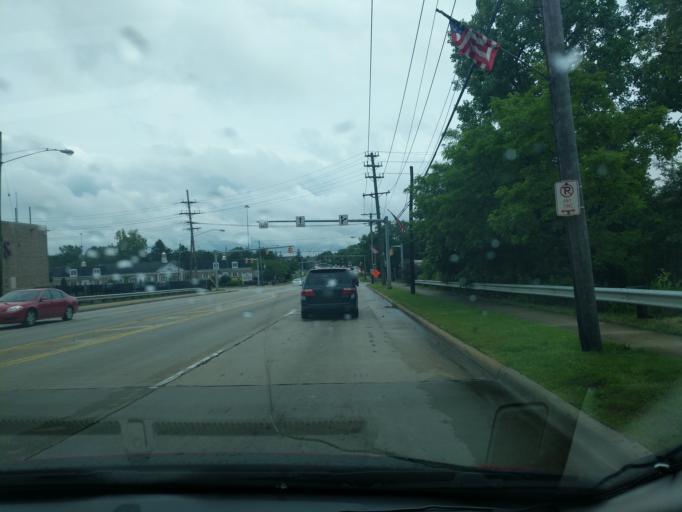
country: US
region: Ohio
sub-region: Cuyahoga County
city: Warrensville Heights
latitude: 41.4278
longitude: -81.5367
